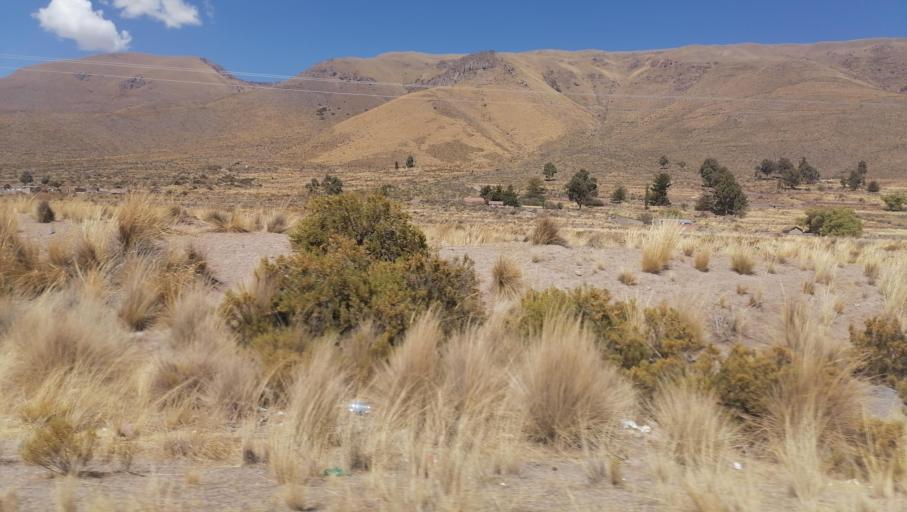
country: BO
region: Oruro
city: Challapata
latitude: -18.9861
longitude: -66.7793
